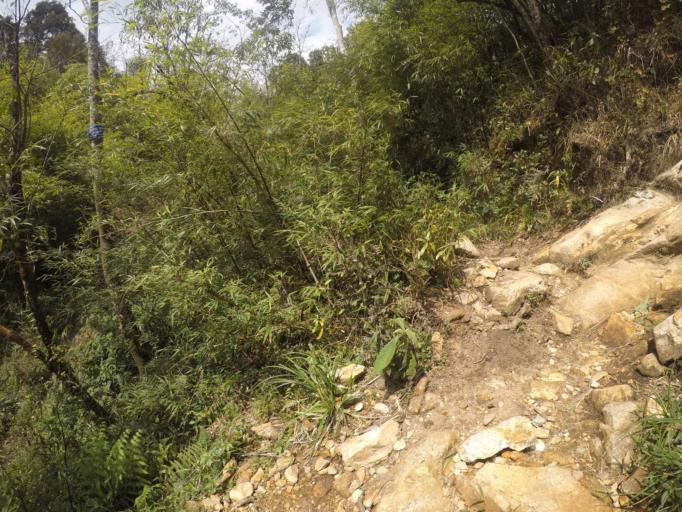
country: VN
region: Lao Cai
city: Sa Pa
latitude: 22.3518
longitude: 103.7747
